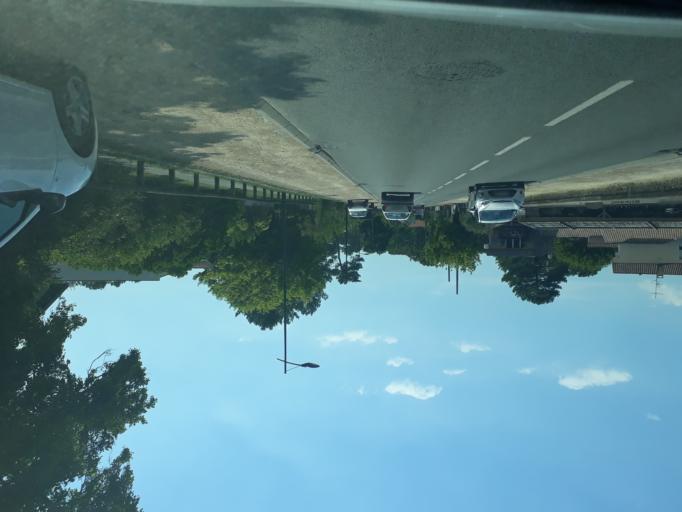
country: FR
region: Aquitaine
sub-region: Departement de la Gironde
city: Ares
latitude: 44.7435
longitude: -1.1819
